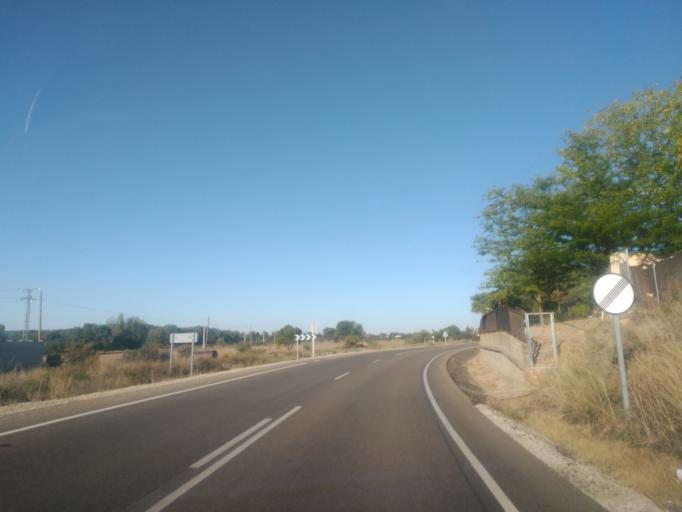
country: ES
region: Castille and Leon
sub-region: Provincia de Burgos
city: Zazuar
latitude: 41.6937
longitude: -3.5459
